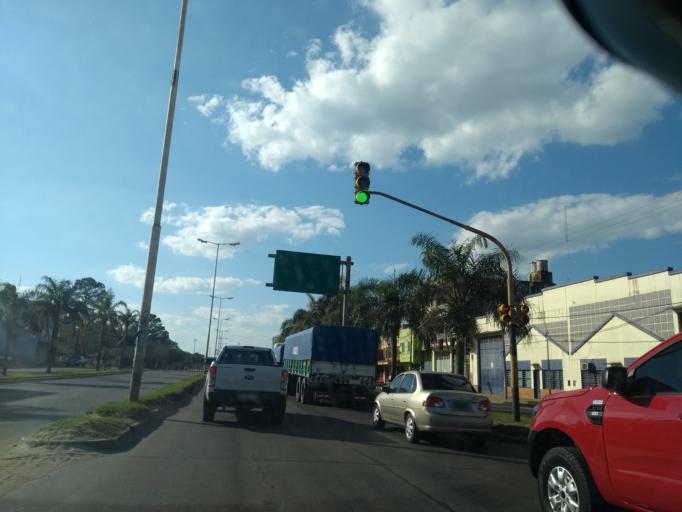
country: AR
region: Corrientes
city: Corrientes
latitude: -27.4839
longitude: -58.7881
